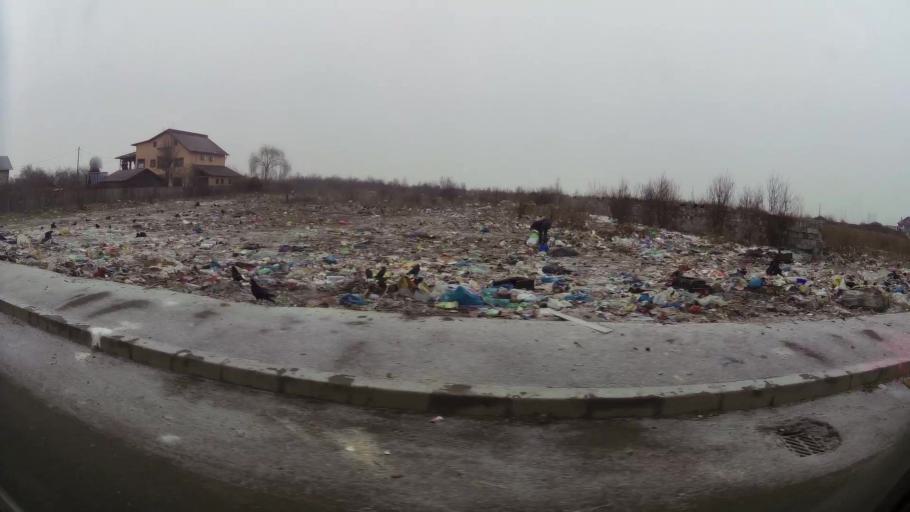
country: RO
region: Prahova
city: Ploiesti
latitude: 44.9514
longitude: 26.0502
